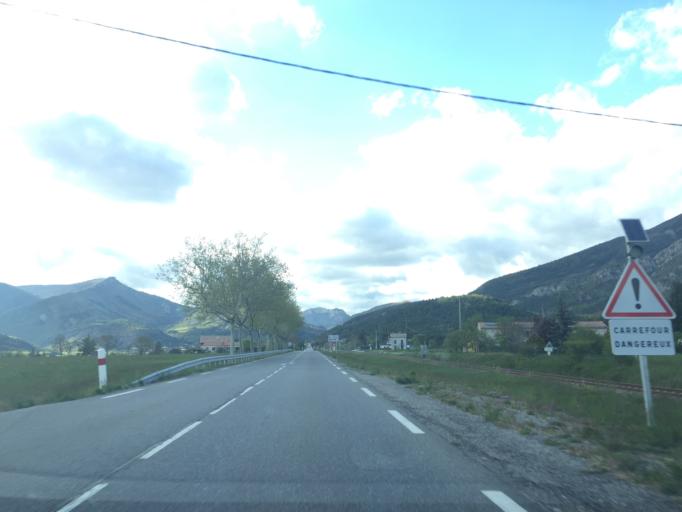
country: FR
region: Provence-Alpes-Cote d'Azur
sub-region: Departement des Hautes-Alpes
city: Serres
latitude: 44.4024
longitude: 5.7324
